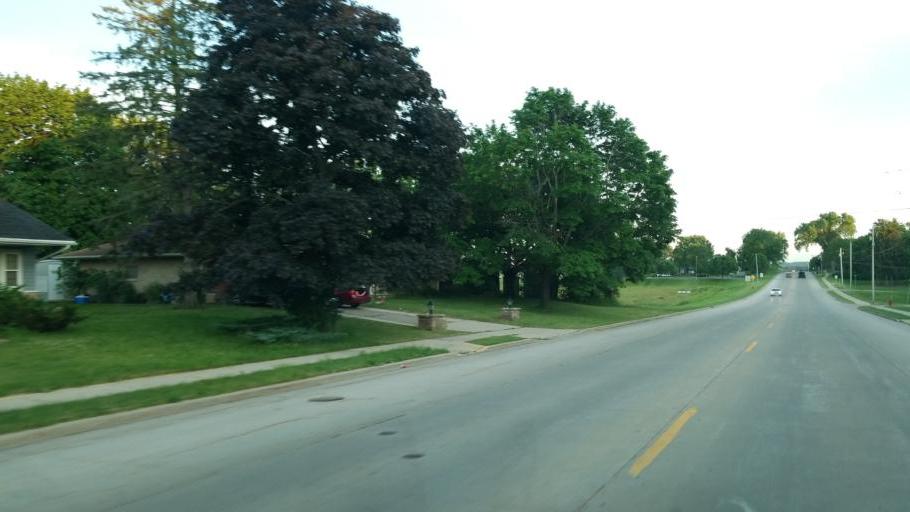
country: US
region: Wisconsin
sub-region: Monroe County
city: Tomah
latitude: 43.9680
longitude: -90.5049
